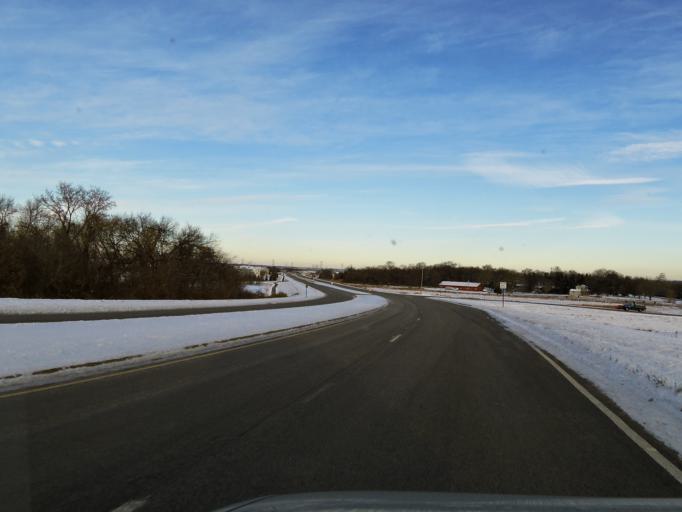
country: US
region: Minnesota
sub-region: Scott County
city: Prior Lake
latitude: 44.7662
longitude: -93.4050
